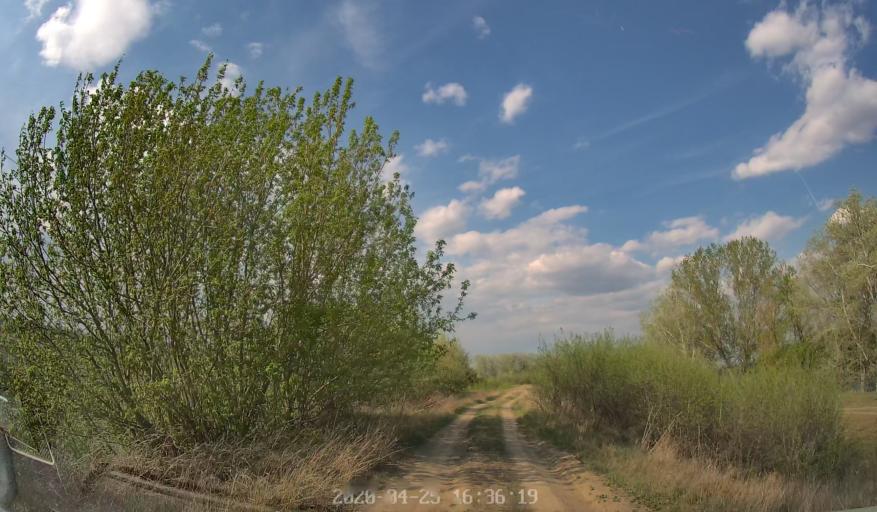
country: MD
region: Chisinau
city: Vadul lui Voda
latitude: 47.1109
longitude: 29.0644
